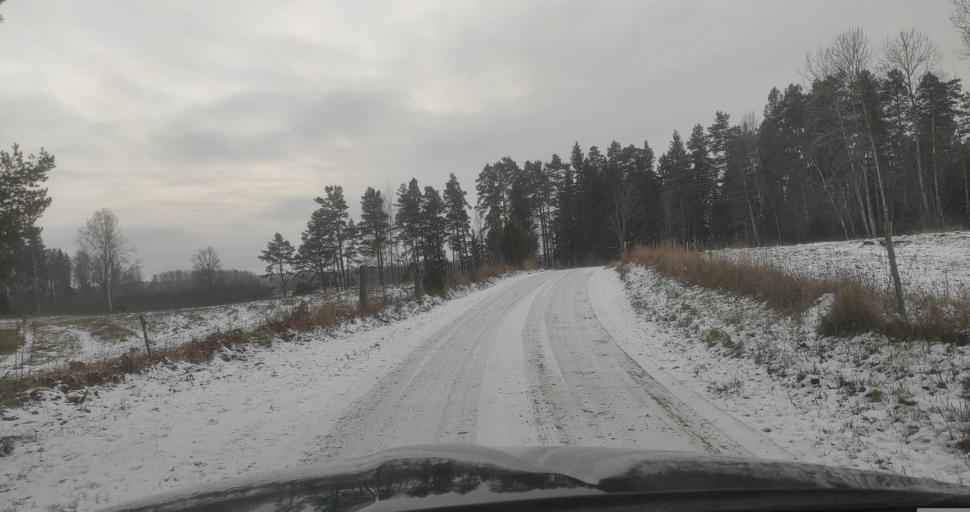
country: LV
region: Kuldigas Rajons
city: Kuldiga
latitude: 56.9938
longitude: 21.8074
